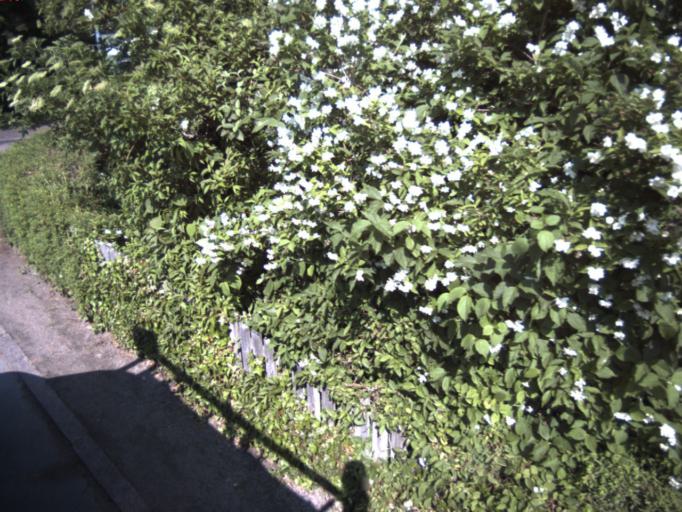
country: SE
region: Skane
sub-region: Helsingborg
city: Helsingborg
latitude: 56.0331
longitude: 12.7334
